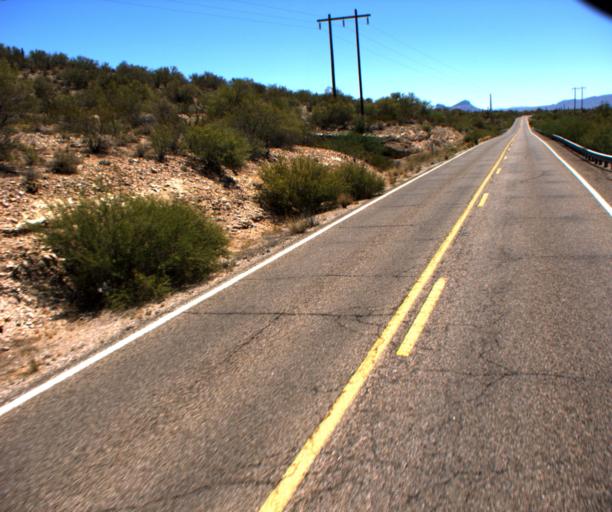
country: US
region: Arizona
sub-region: Pinal County
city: Kearny
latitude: 33.0227
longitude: -110.8580
